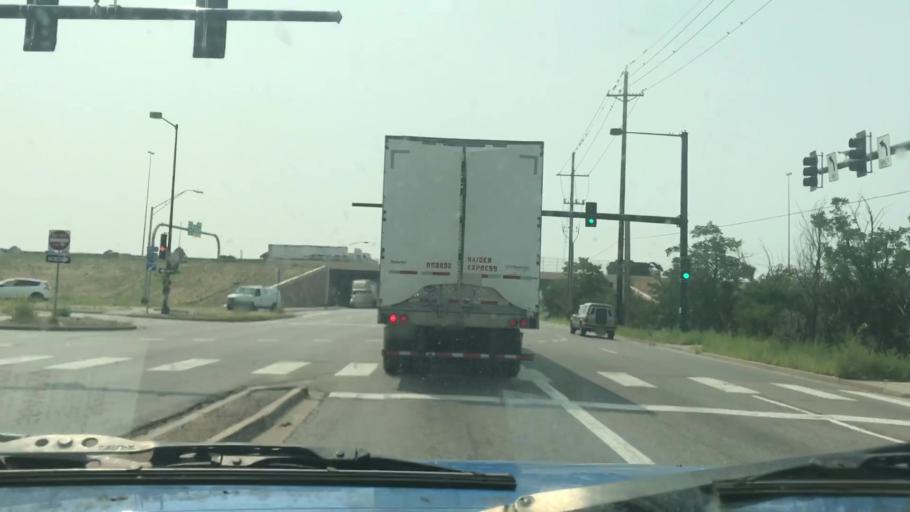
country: US
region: Colorado
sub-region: Adams County
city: Aurora
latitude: 39.7773
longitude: -104.8659
